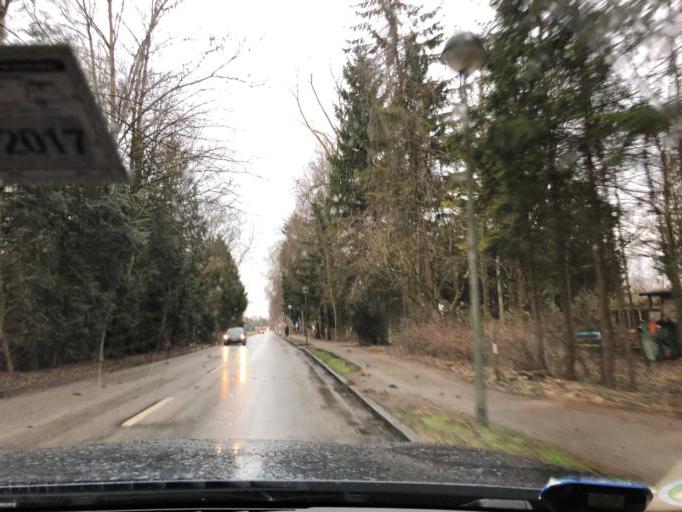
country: DE
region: Bavaria
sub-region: Upper Bavaria
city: Grobenzell
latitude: 48.1982
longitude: 11.3901
